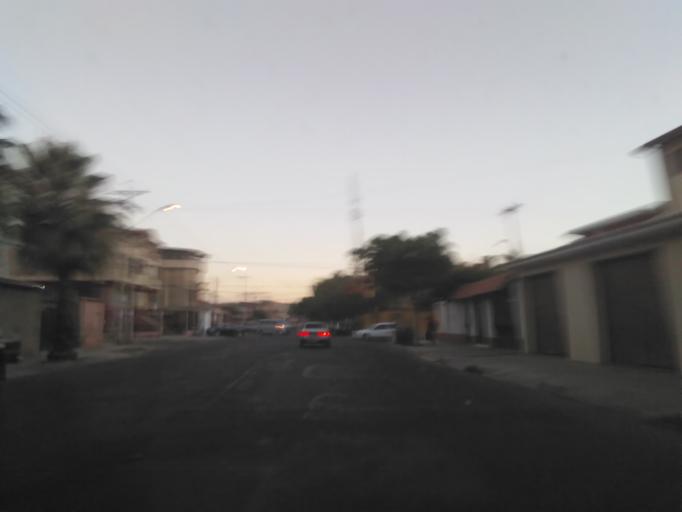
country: BO
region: Cochabamba
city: Cochabamba
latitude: -17.3814
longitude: -66.1695
